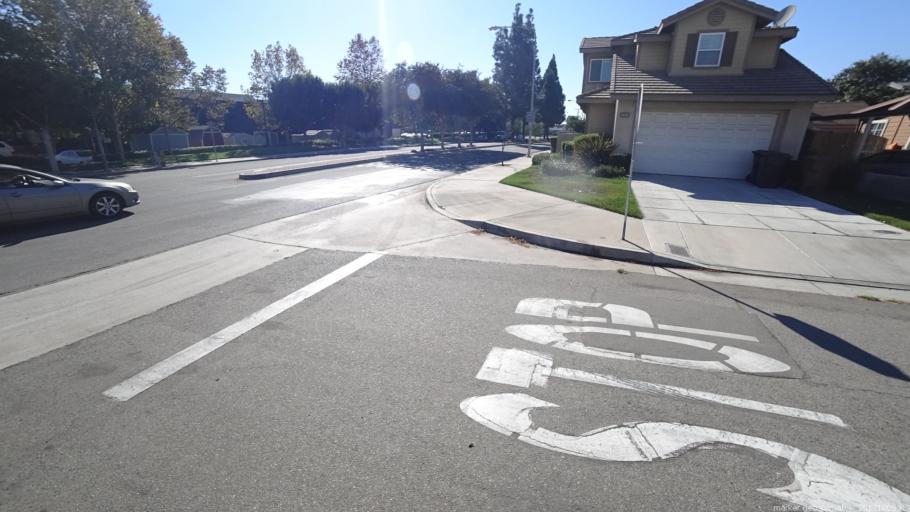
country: US
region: California
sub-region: Orange County
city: Garden Grove
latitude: 33.7761
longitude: -117.9437
